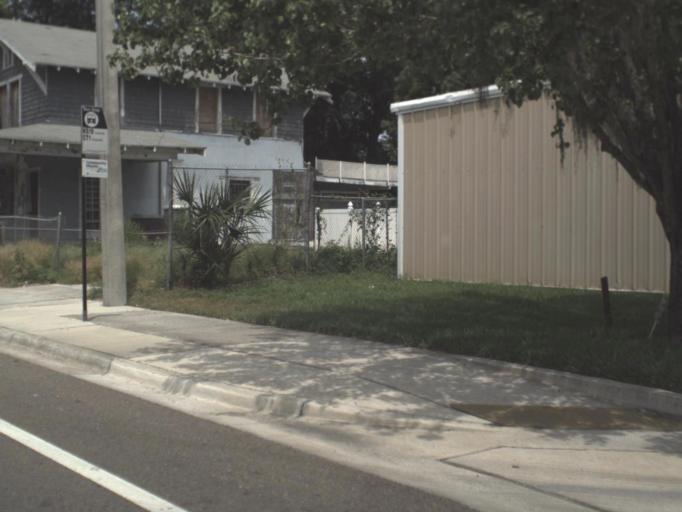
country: US
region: Florida
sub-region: Duval County
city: Jacksonville
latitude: 30.3857
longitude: -81.6487
